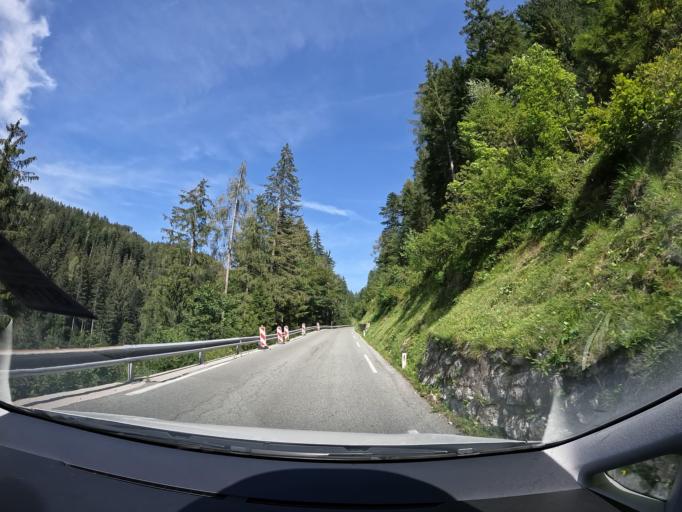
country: AT
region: Carinthia
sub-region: Politischer Bezirk Villach Land
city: Sankt Jakob
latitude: 46.5398
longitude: 14.0866
